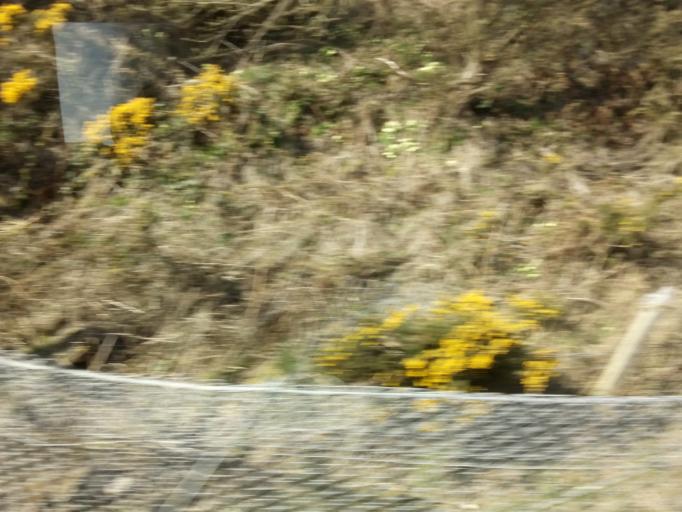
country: GB
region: Scotland
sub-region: The Scottish Borders
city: Eyemouth
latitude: 55.8327
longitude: -2.0601
